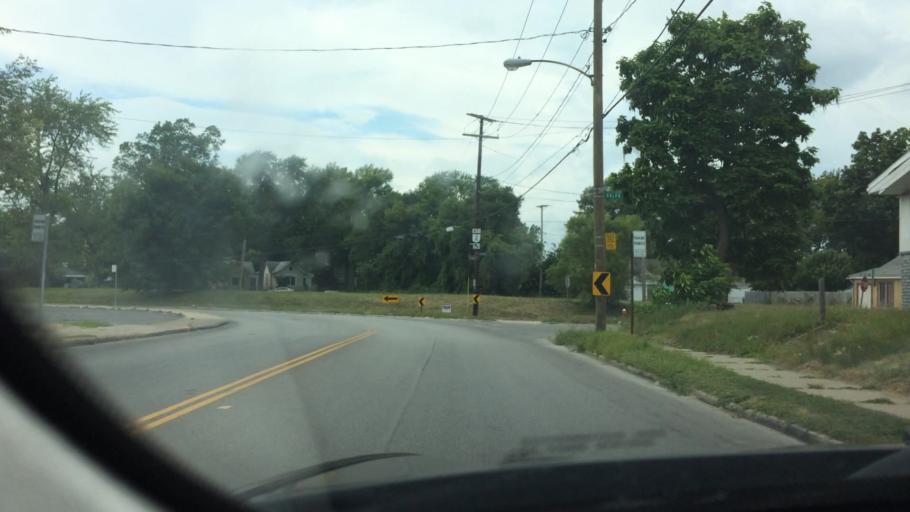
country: US
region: Ohio
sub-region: Wood County
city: Rossford
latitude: 41.6357
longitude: -83.5837
